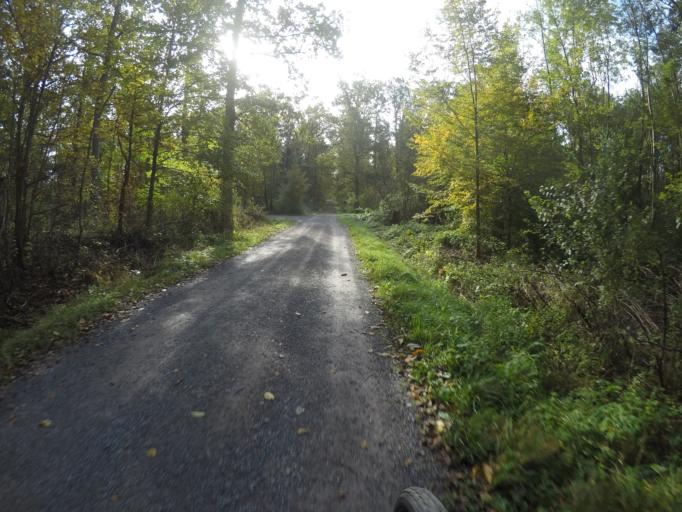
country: DE
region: Baden-Wuerttemberg
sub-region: Regierungsbezirk Stuttgart
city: Ehningen
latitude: 48.6754
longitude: 8.9582
